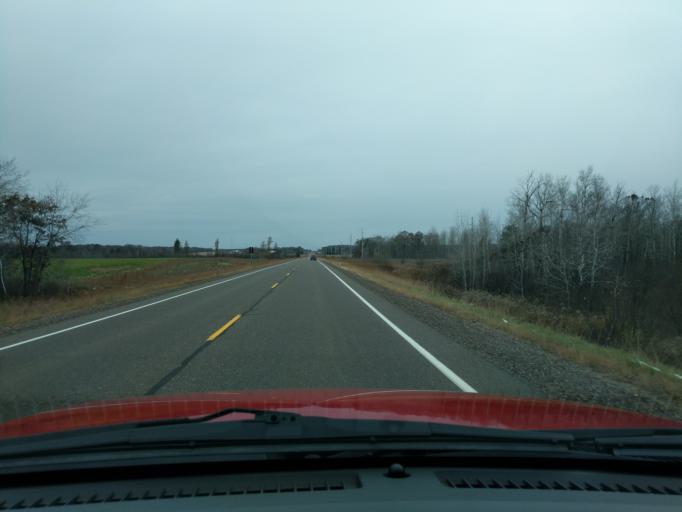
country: US
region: Wisconsin
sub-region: Washburn County
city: Shell Lake
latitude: 45.8156
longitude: -92.0960
